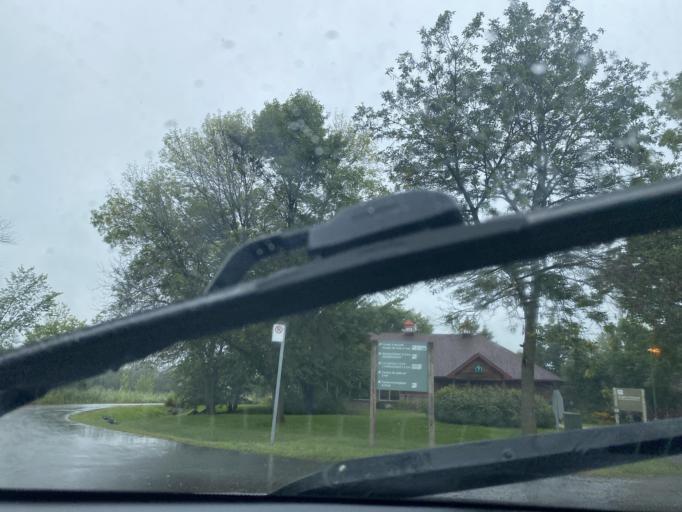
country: CA
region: Quebec
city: Baie-D'Urfe
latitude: 45.4617
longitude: -73.9207
